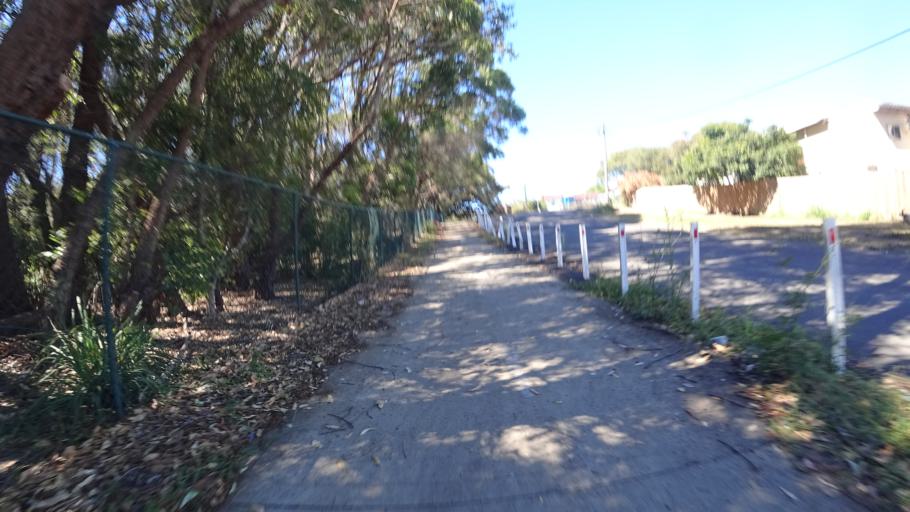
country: AU
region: New South Wales
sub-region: Rockdale
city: Arncliffe
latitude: -33.9403
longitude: 151.1538
